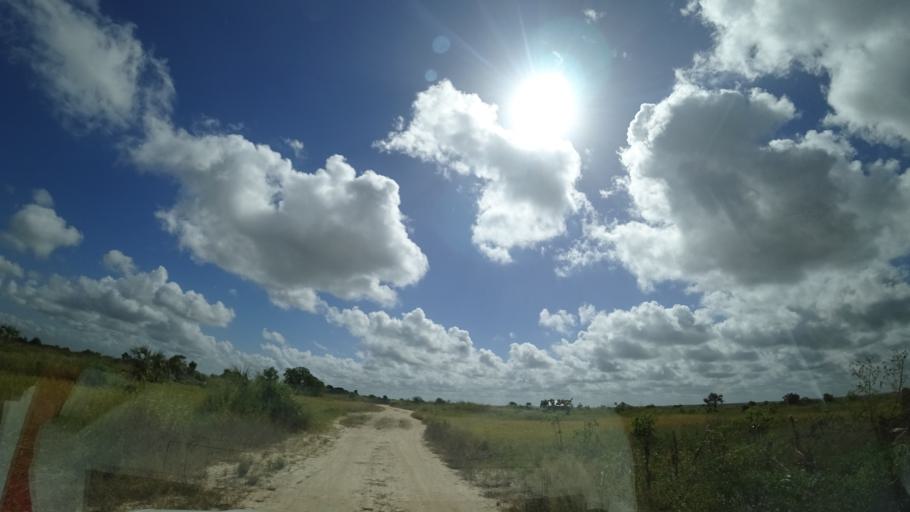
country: MZ
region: Sofala
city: Dondo
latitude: -19.4195
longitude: 34.5648
